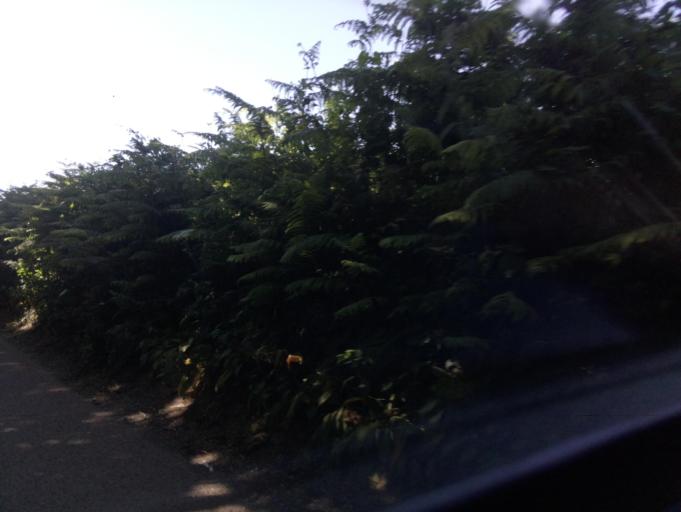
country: GB
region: England
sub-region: Borough of Torbay
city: Brixham
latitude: 50.3937
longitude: -3.5373
